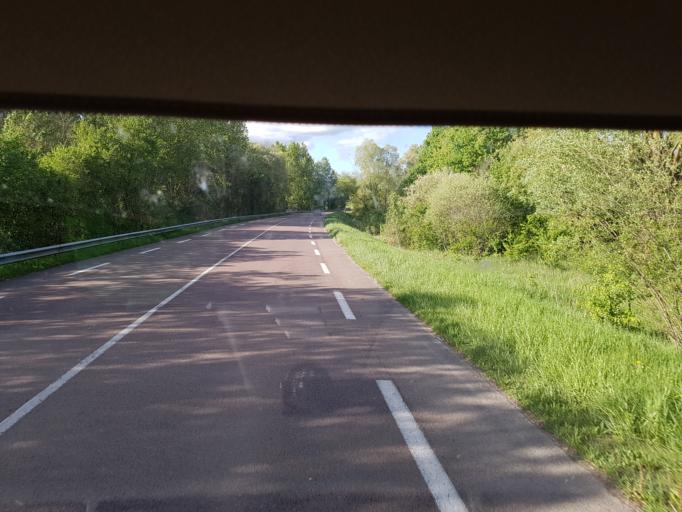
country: FR
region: Bourgogne
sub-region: Departement de l'Yonne
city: Saint-Florentin
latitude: 47.9992
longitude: 3.7354
